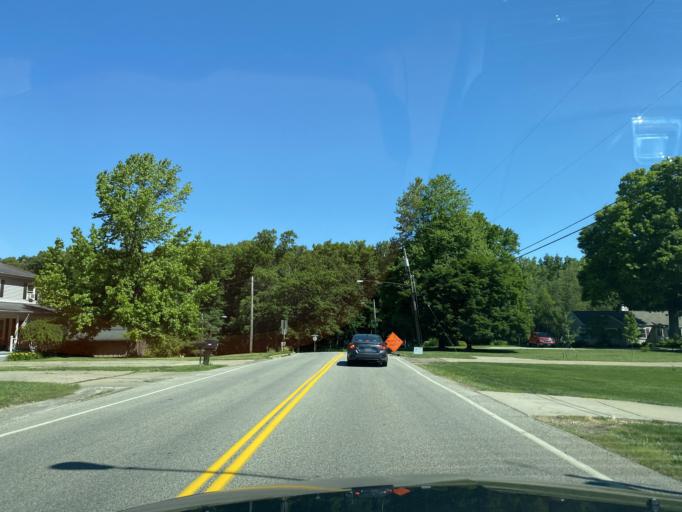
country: US
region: Ohio
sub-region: Summit County
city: Akron
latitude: 41.1255
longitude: -81.5497
